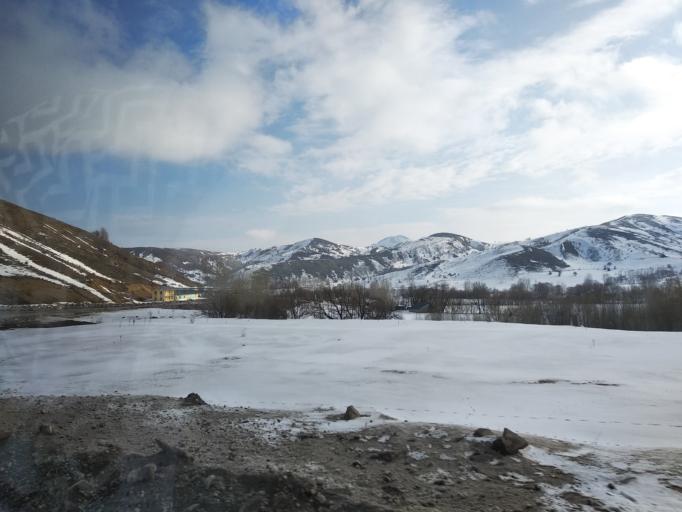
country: TR
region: Erzincan
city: Catalarmut
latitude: 39.9053
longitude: 39.3991
